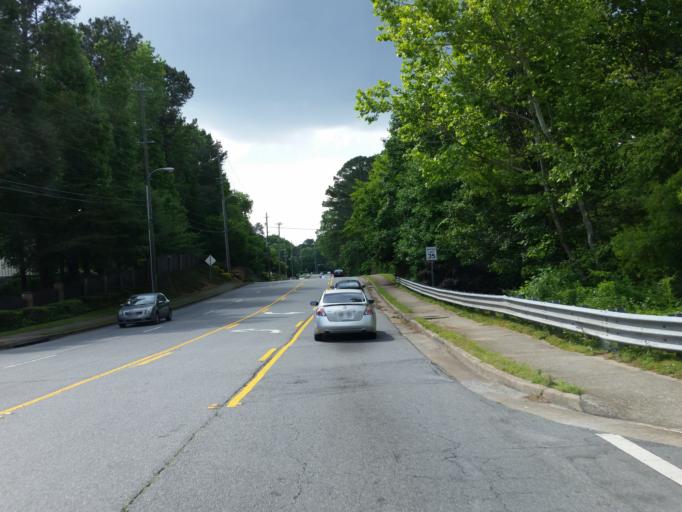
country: US
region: Georgia
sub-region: Cobb County
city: Smyrna
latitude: 33.9314
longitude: -84.4767
